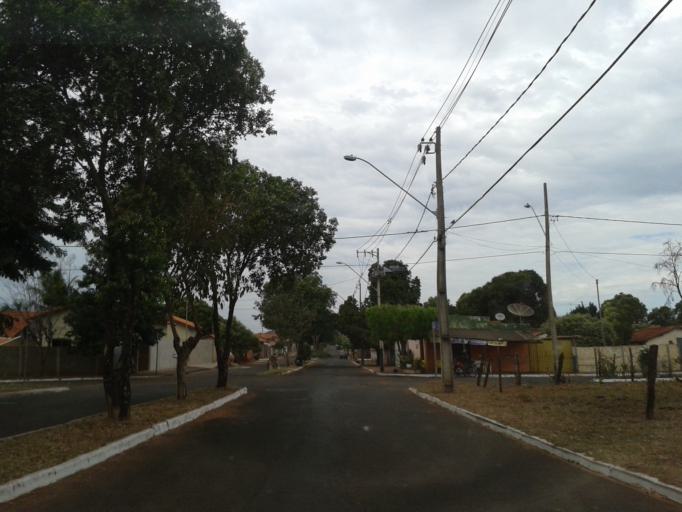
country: BR
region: Minas Gerais
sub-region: Santa Vitoria
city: Santa Vitoria
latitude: -18.8496
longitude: -50.1197
